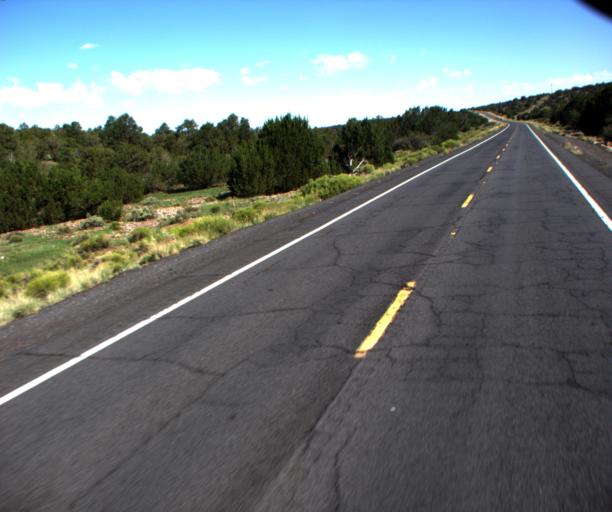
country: US
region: Arizona
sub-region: Coconino County
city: Williams
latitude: 35.4616
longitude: -112.1717
